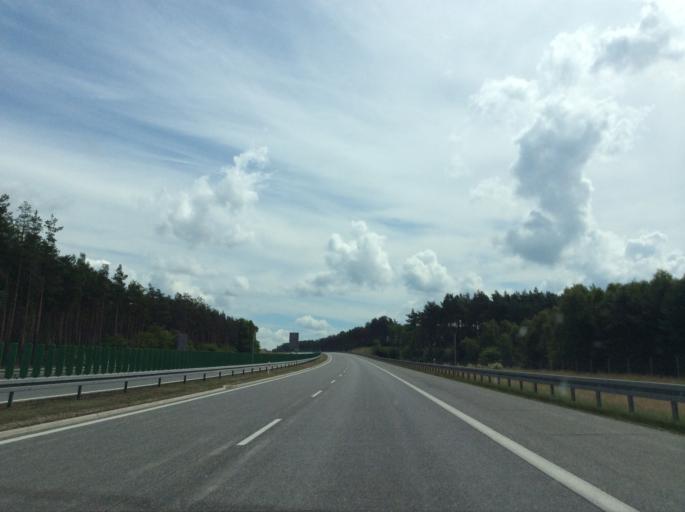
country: PL
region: Lubusz
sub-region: Powiat slubicki
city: Rzepin
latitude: 52.3340
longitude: 14.9169
